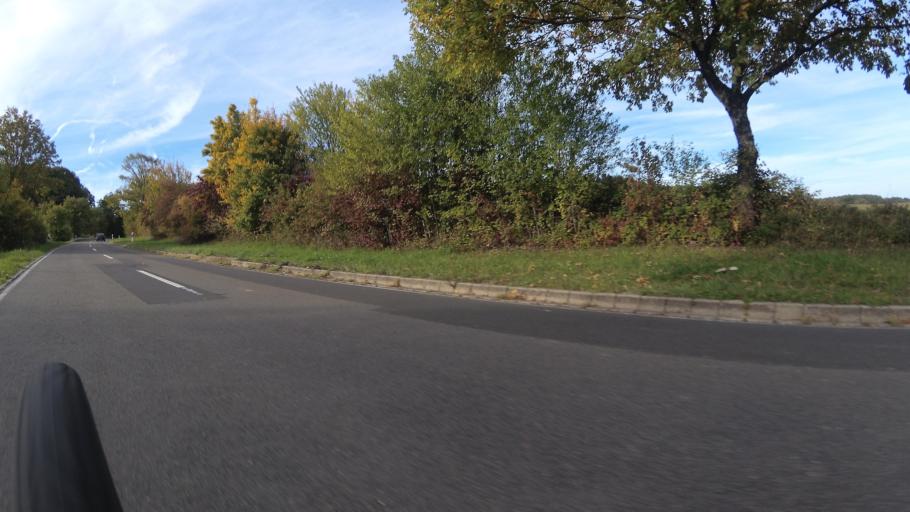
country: DE
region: Rheinland-Pfalz
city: Borsborn
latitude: 49.4444
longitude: 7.3924
